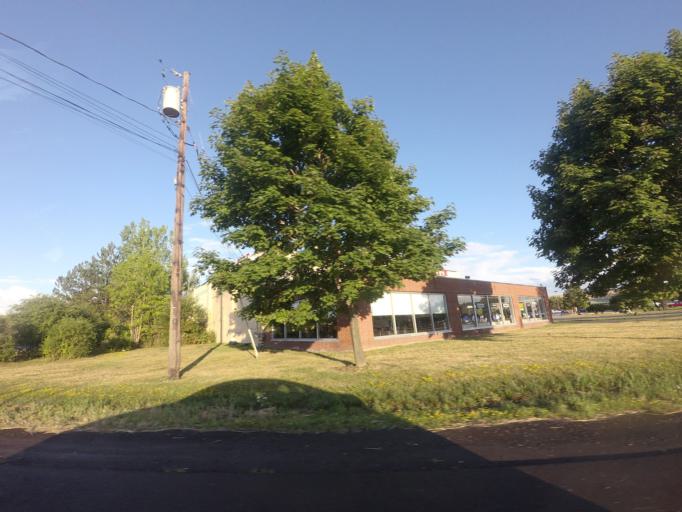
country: US
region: New York
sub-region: Onondaga County
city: East Syracuse
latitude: 43.0536
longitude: -76.0679
